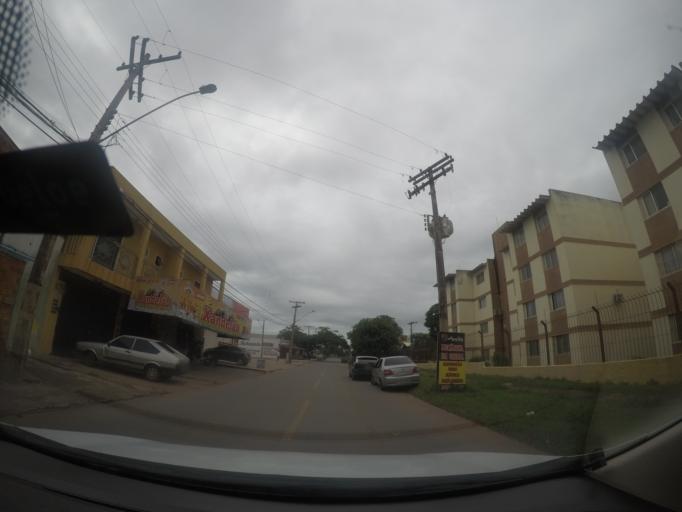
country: BR
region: Goias
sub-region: Goiania
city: Goiania
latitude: -16.6969
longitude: -49.3243
